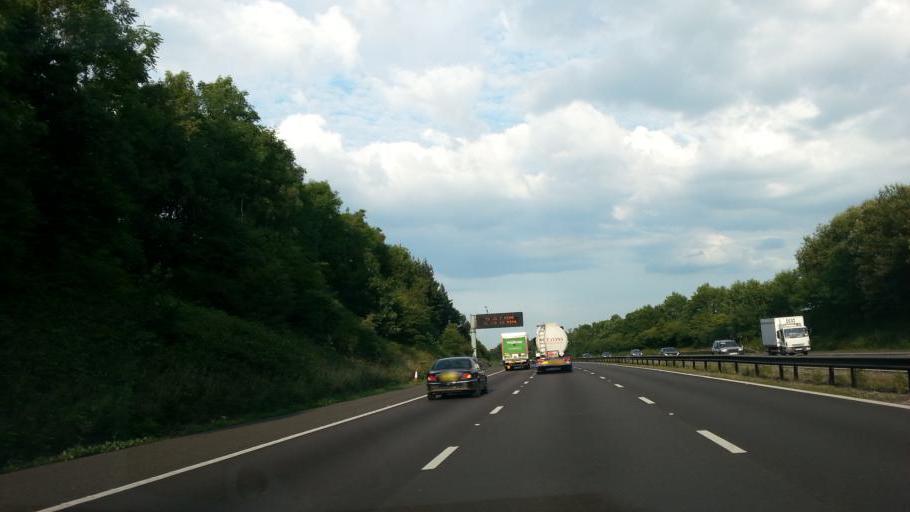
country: GB
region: England
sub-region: Worcestershire
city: Barnt Green
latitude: 52.3536
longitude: -2.0095
